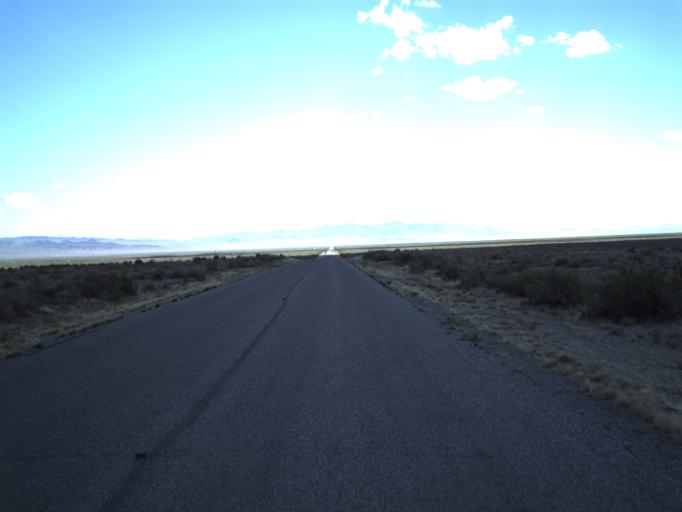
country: US
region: Nevada
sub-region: White Pine County
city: McGill
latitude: 39.0536
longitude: -114.0029
